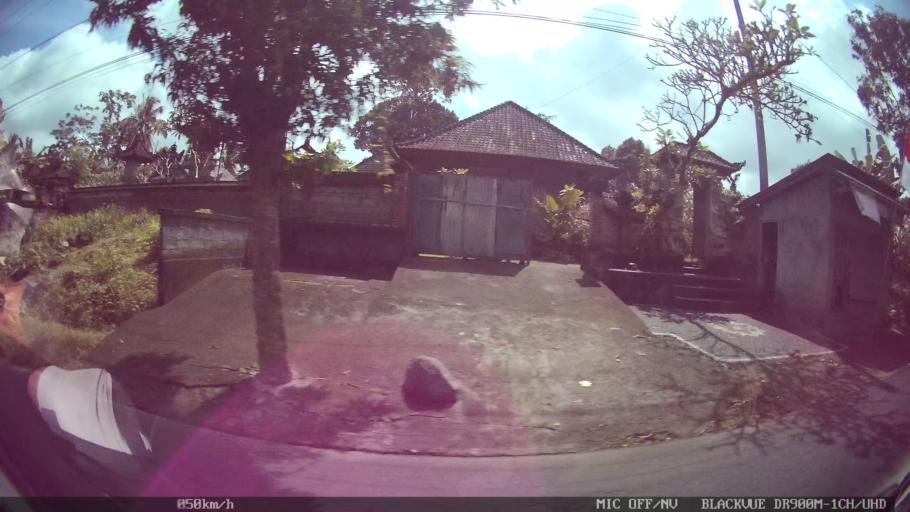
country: ID
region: Bali
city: Banjar Mulung
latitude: -8.4940
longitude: 115.3205
